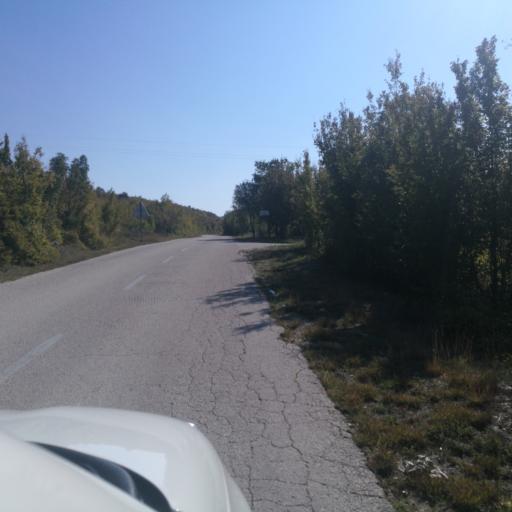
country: HR
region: Splitsko-Dalmatinska
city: Trilj
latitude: 43.5234
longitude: 16.7491
